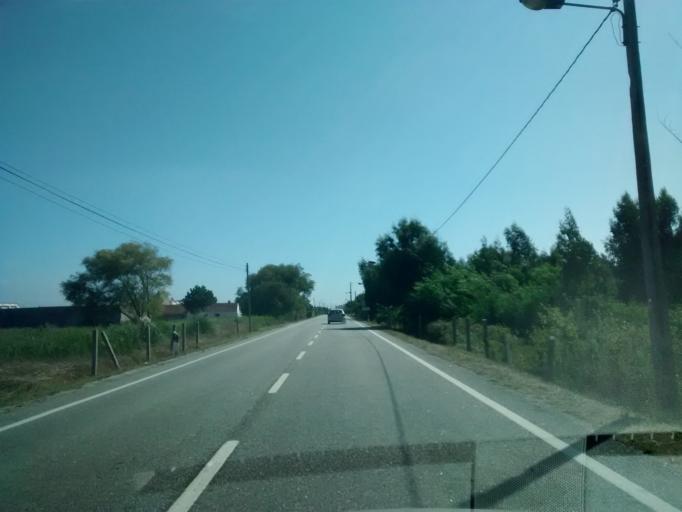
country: PT
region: Aveiro
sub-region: Ilhavo
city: Gafanha da Nazare
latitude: 40.6689
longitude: -8.7262
